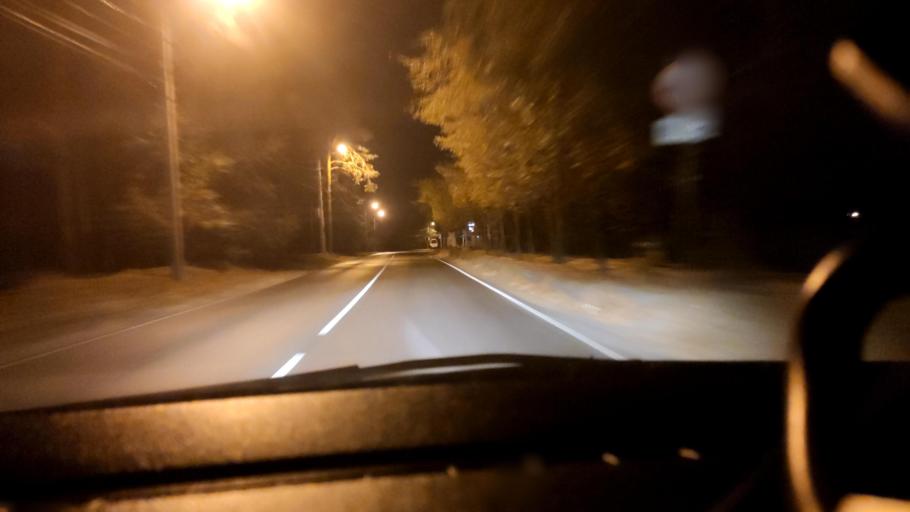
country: RU
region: Voronezj
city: Pridonskoy
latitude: 51.6472
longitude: 39.0983
